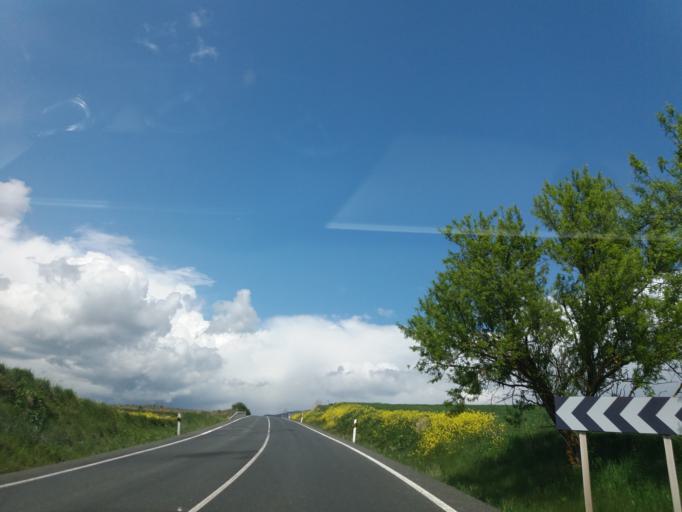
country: ES
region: La Rioja
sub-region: Provincia de La Rioja
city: Fonzaleche
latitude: 42.5820
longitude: -3.0268
